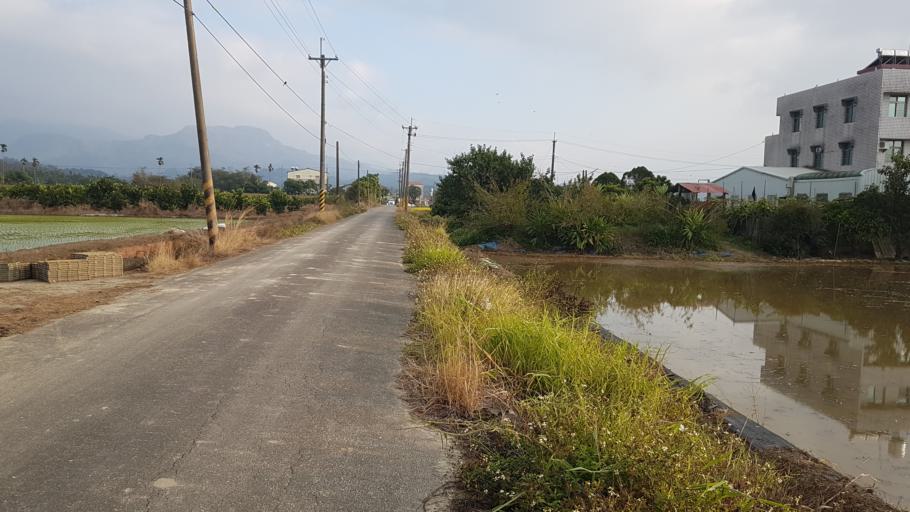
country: TW
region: Taiwan
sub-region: Chiayi
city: Jiayi Shi
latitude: 23.3736
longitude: 120.4541
